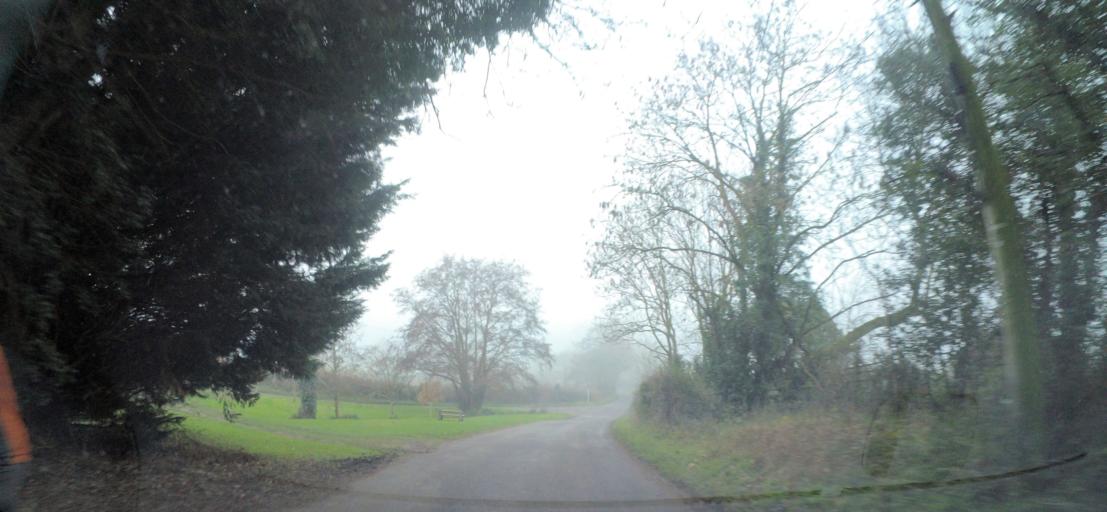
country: GB
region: England
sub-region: West Berkshire
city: Theale
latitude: 51.4099
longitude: -1.1030
